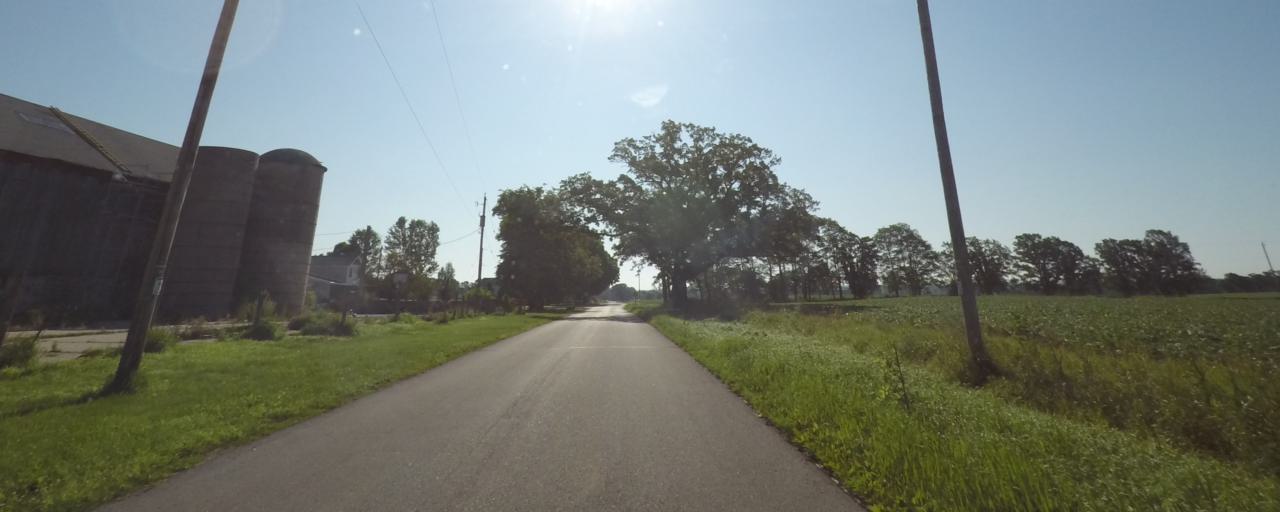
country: US
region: Wisconsin
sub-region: Jefferson County
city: Palmyra
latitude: 42.9152
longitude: -88.5736
